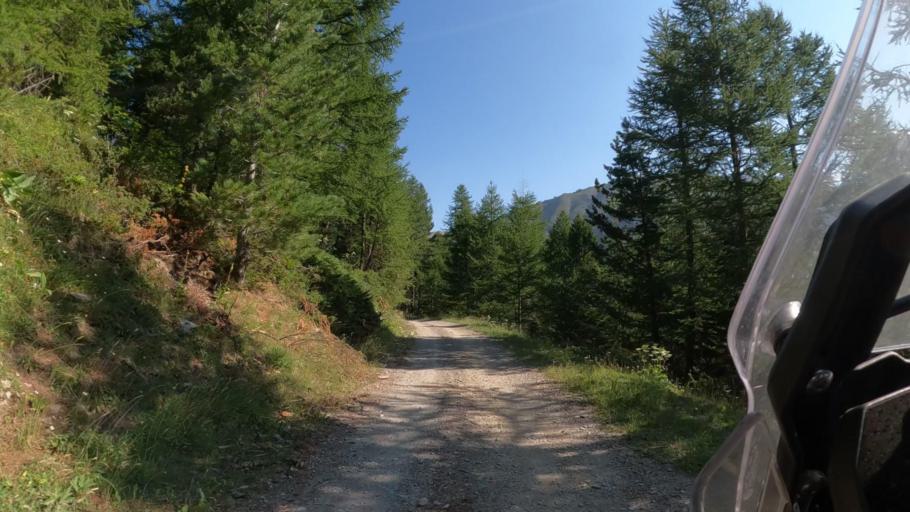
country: FR
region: Provence-Alpes-Cote d'Azur
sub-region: Departement des Hautes-Alpes
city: Guillestre
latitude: 44.5860
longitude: 6.6096
